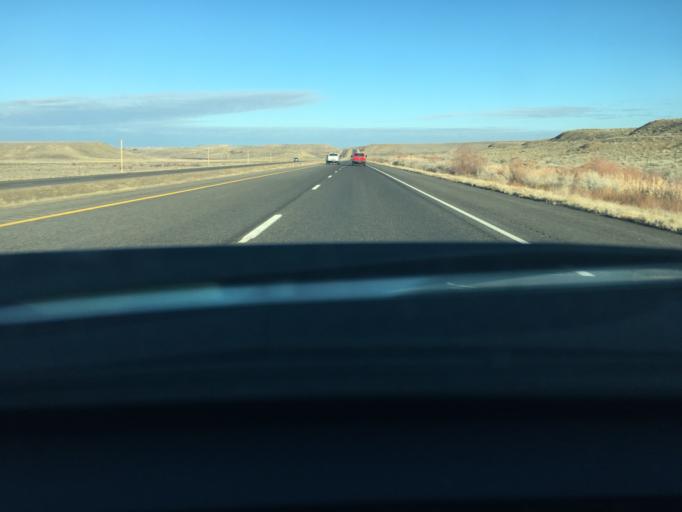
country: US
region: Colorado
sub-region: Mesa County
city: Clifton
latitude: 38.9121
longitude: -108.3745
